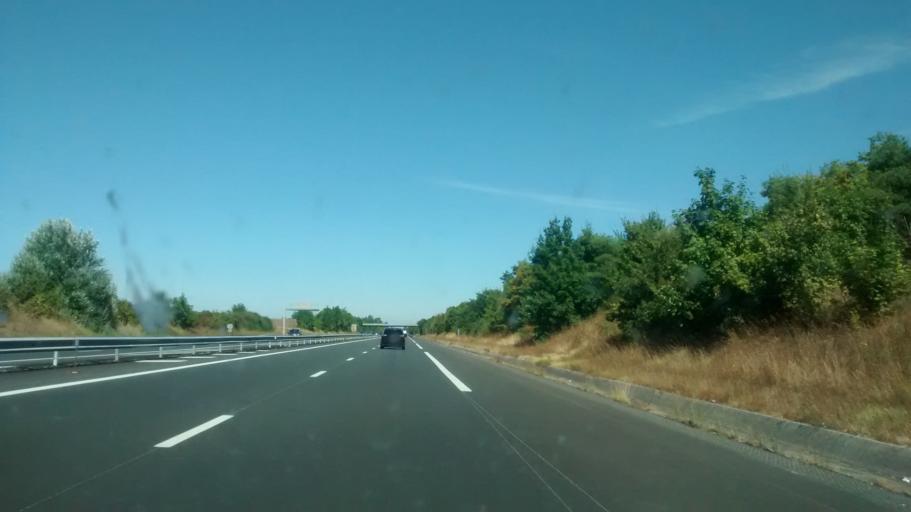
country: FR
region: Poitou-Charentes
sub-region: Departement des Deux-Sevres
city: Beauvoir-sur-Niort
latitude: 46.1193
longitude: -0.5327
